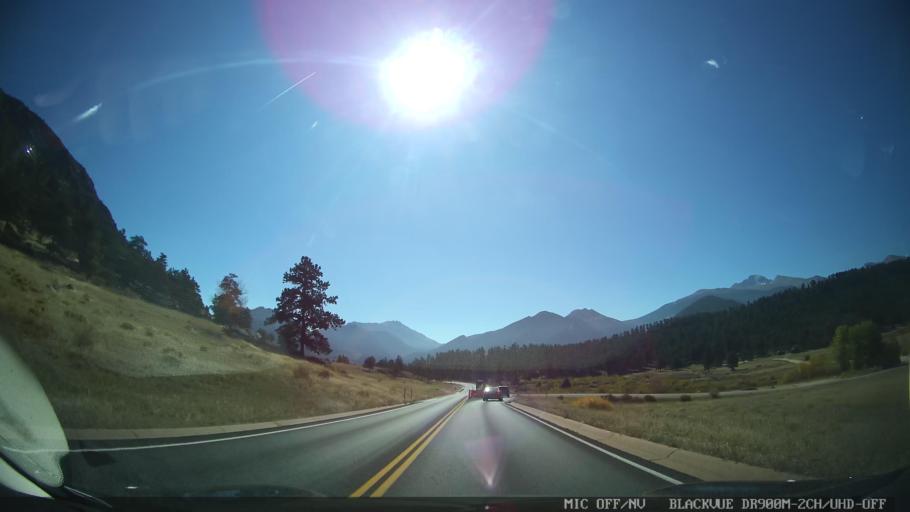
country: US
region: Colorado
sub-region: Larimer County
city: Estes Park
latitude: 40.3540
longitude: -105.5843
